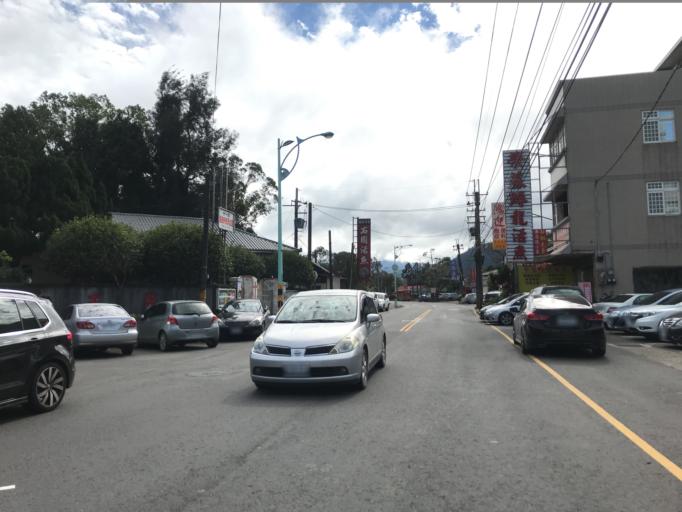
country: TW
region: Taiwan
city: Daxi
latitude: 24.8396
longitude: 121.2404
